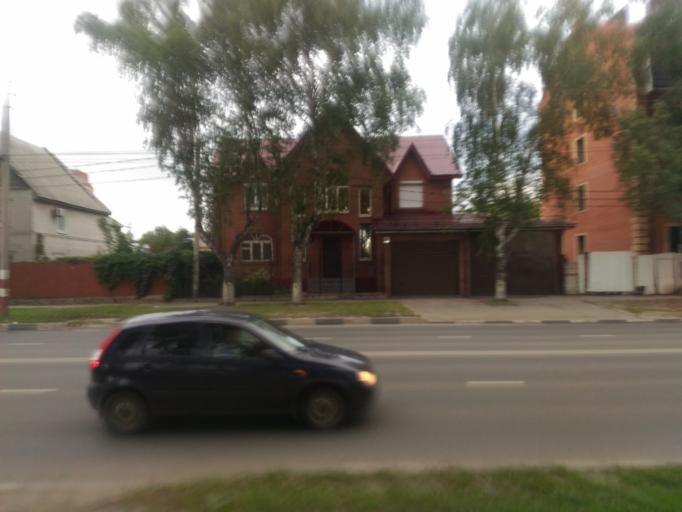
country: RU
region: Ulyanovsk
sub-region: Ulyanovskiy Rayon
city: Ulyanovsk
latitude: 54.2751
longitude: 48.3346
